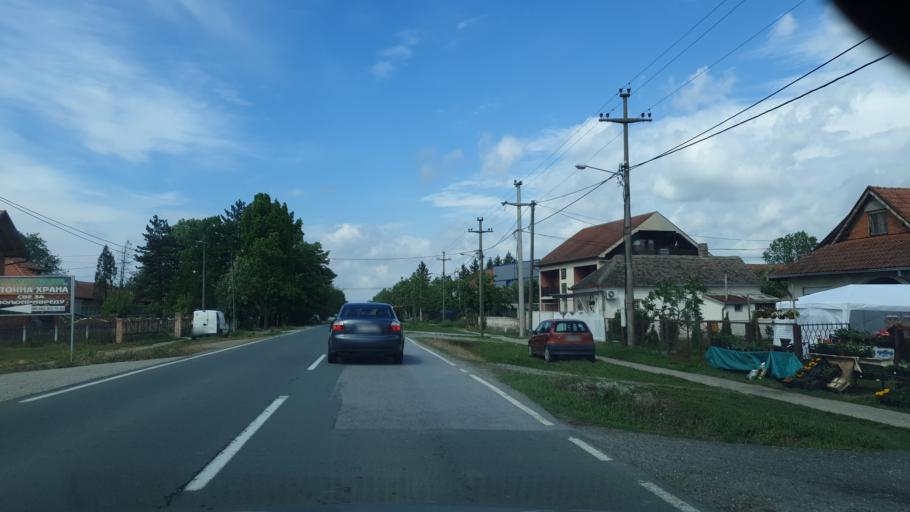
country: RS
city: Stubline
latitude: 44.5693
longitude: 20.1499
